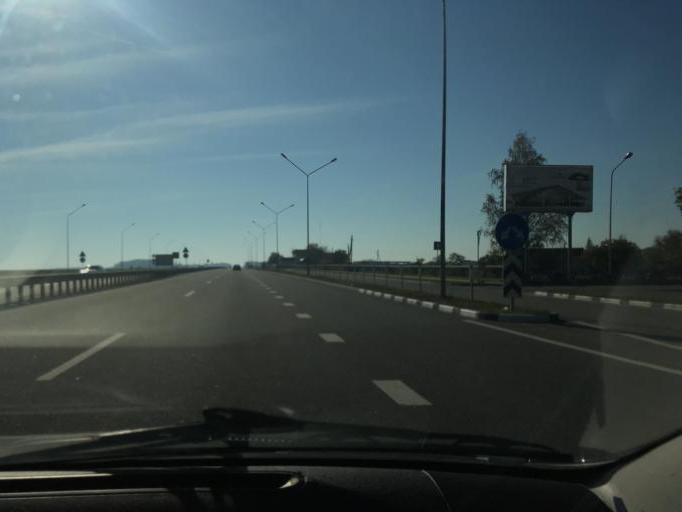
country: BY
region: Minsk
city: Slutsk
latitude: 53.2202
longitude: 27.5505
